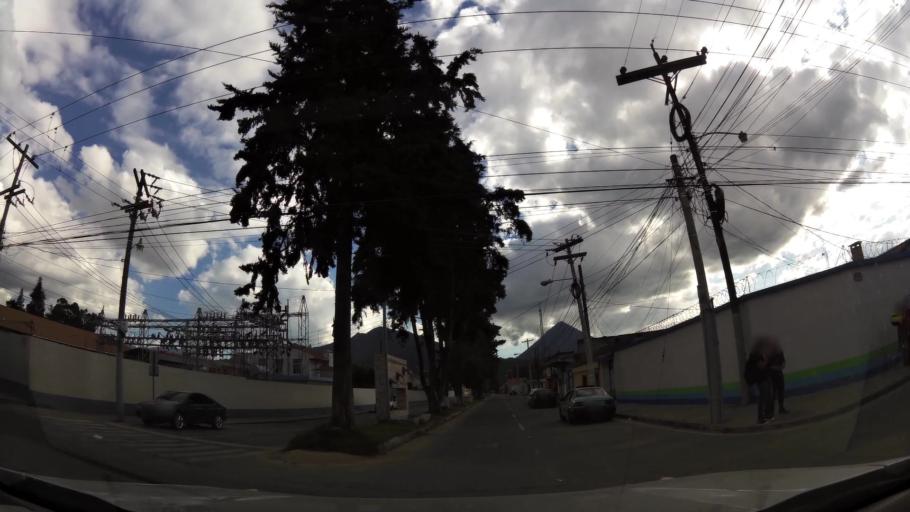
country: GT
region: Quetzaltenango
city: Quetzaltenango
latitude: 14.8476
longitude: -91.5248
